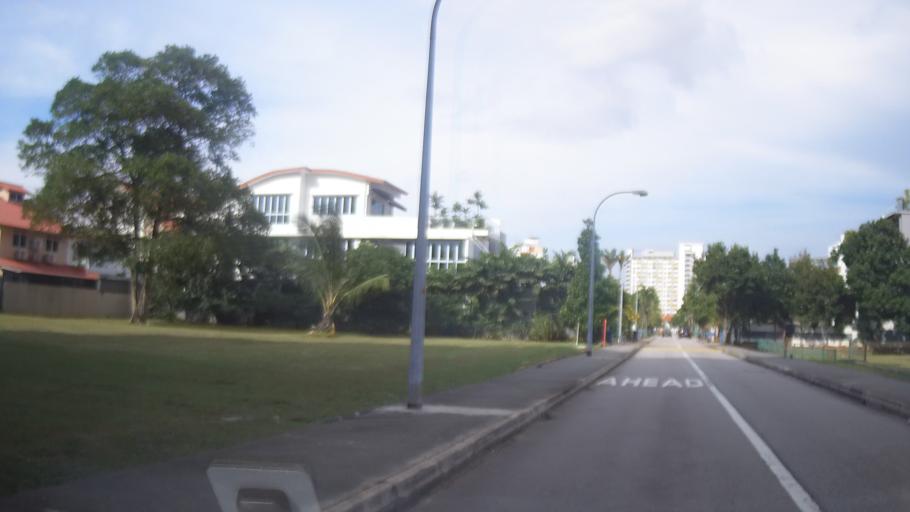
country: SG
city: Singapore
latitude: 1.3285
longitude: 103.8820
